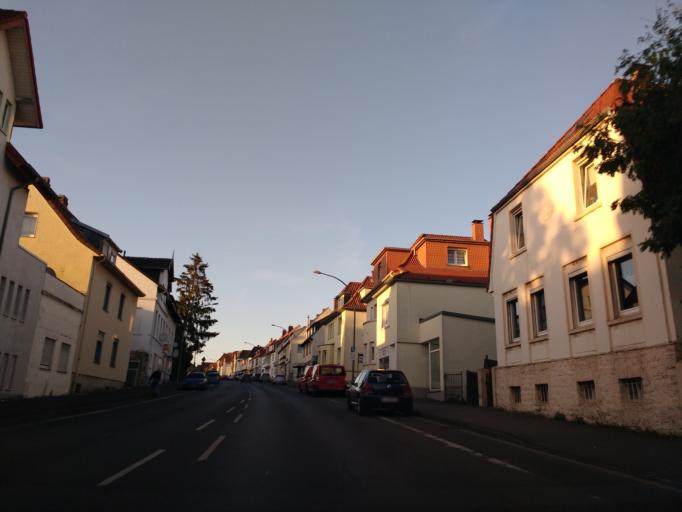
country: DE
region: North Rhine-Westphalia
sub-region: Regierungsbezirk Detmold
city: Detmold
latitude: 51.9444
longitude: 8.8789
